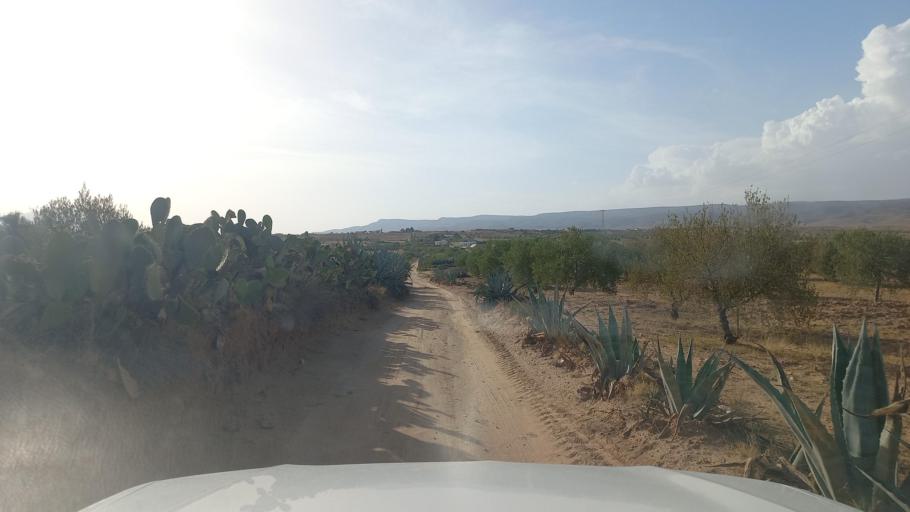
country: TN
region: Al Qasrayn
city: Kasserine
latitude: 35.2359
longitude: 8.9169
